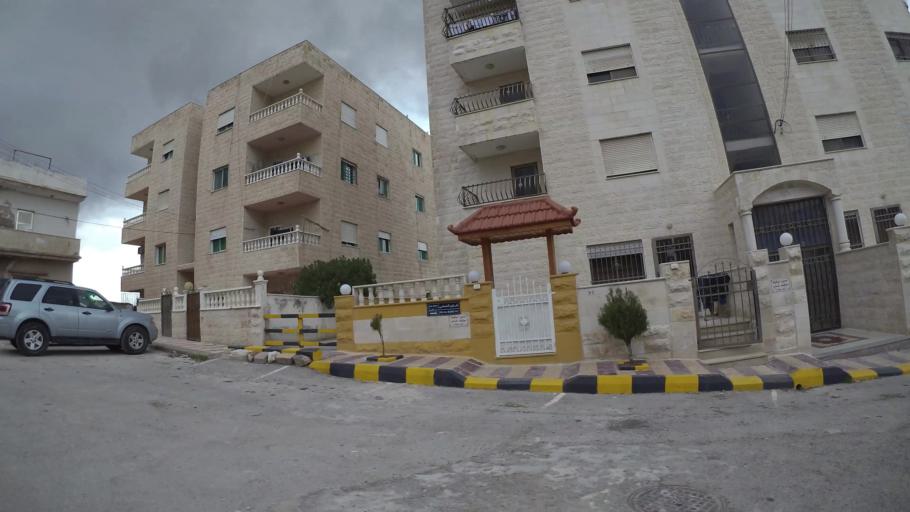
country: JO
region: Amman
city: Amman
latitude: 32.0103
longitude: 35.9487
